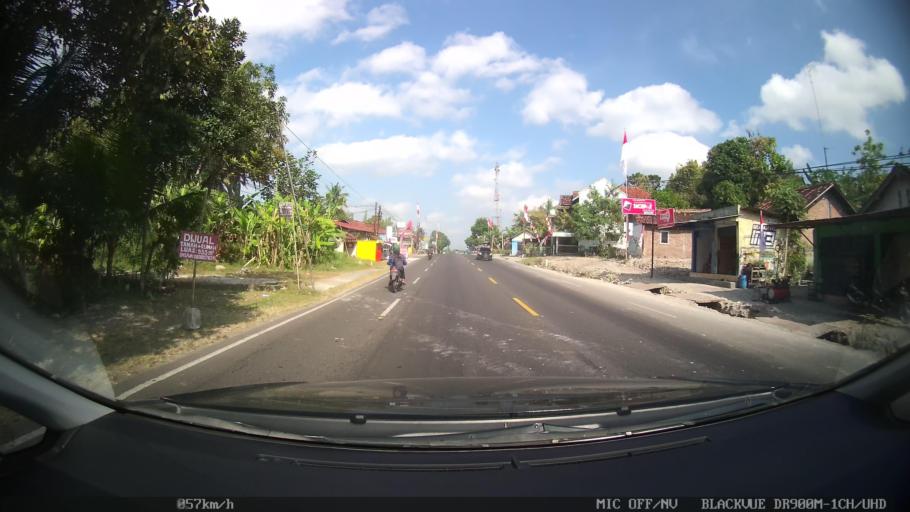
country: ID
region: Daerah Istimewa Yogyakarta
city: Godean
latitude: -7.8130
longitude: 110.2651
